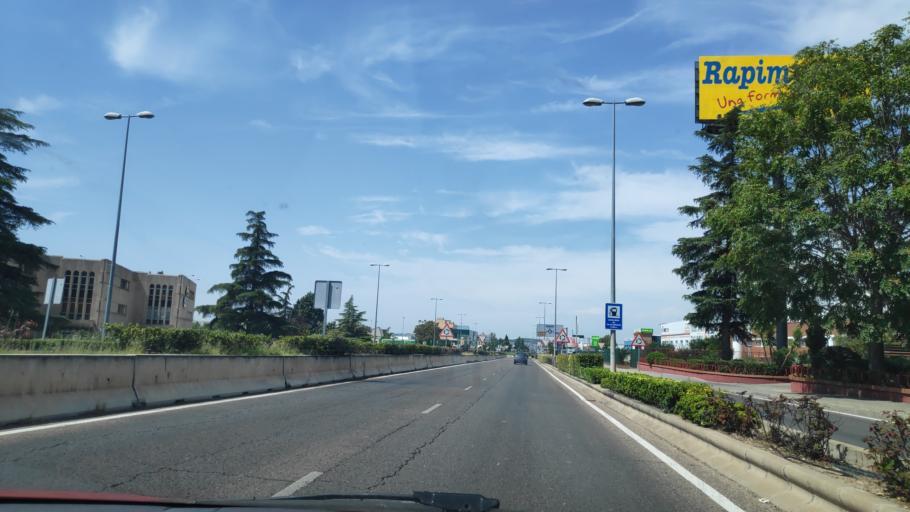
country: ES
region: Madrid
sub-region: Provincia de Madrid
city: Arganda
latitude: 40.3057
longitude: -3.4607
